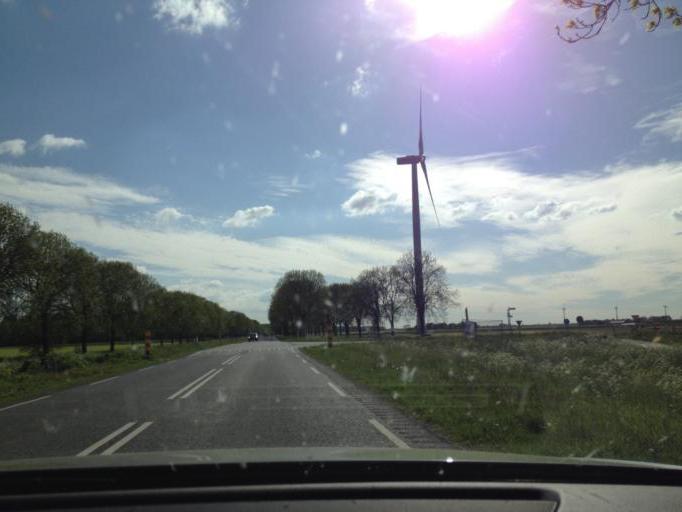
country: NL
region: Utrecht
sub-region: Gemeente Bunschoten
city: Bunschoten
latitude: 52.2750
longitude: 5.4127
